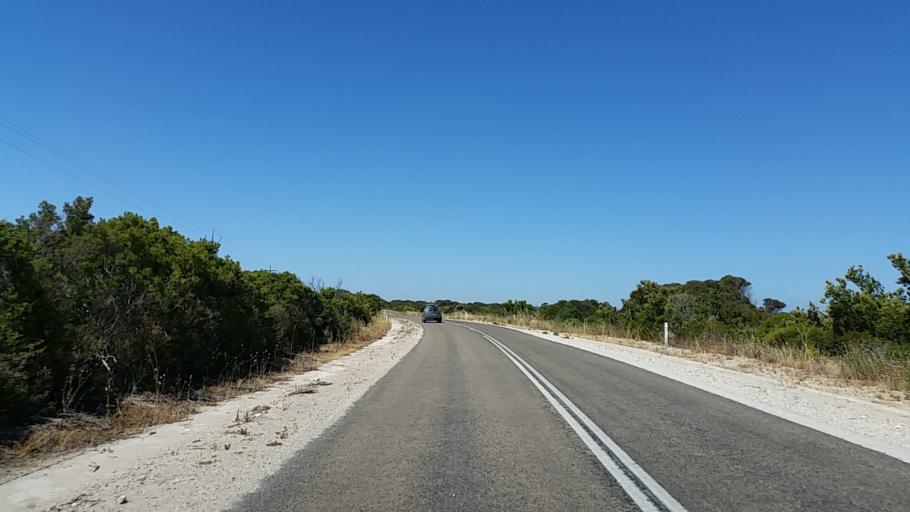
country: AU
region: South Australia
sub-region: Yorke Peninsula
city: Honiton
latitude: -35.2237
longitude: 136.9923
